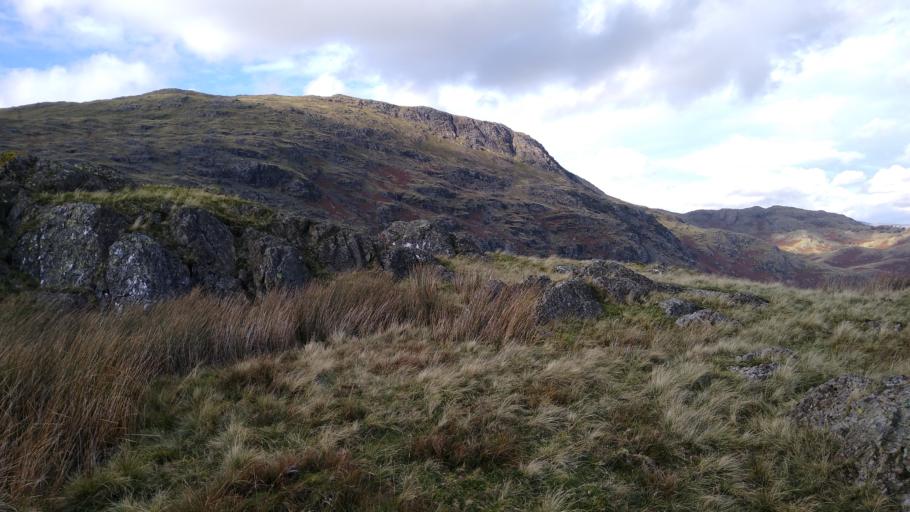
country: GB
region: England
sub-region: Cumbria
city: Ambleside
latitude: 54.3843
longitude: -3.0804
